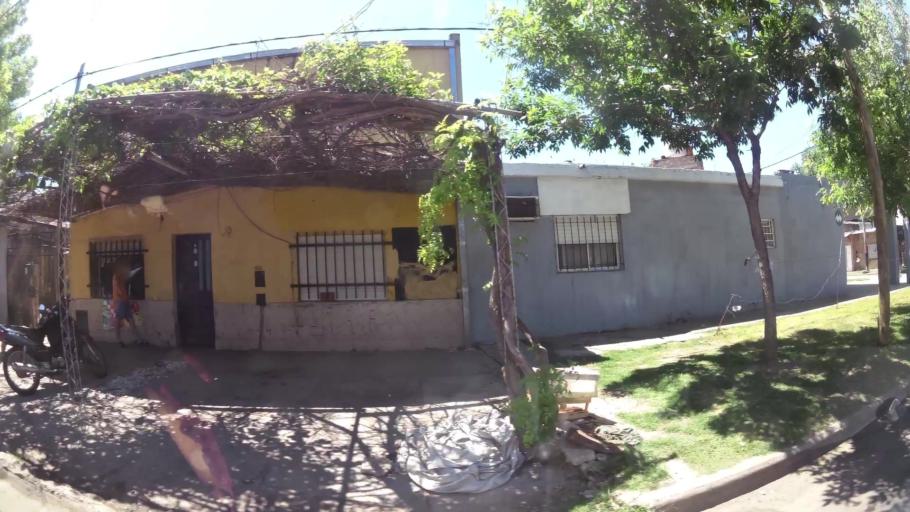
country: AR
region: Santa Fe
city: Perez
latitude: -32.9497
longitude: -60.7191
